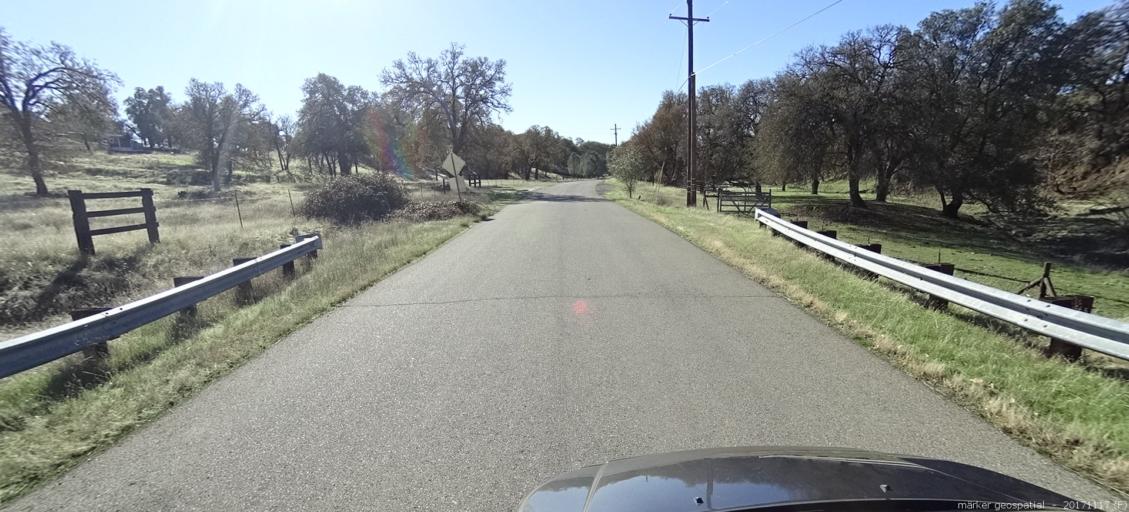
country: US
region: California
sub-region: Shasta County
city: Cottonwood
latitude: 40.4215
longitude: -122.1910
